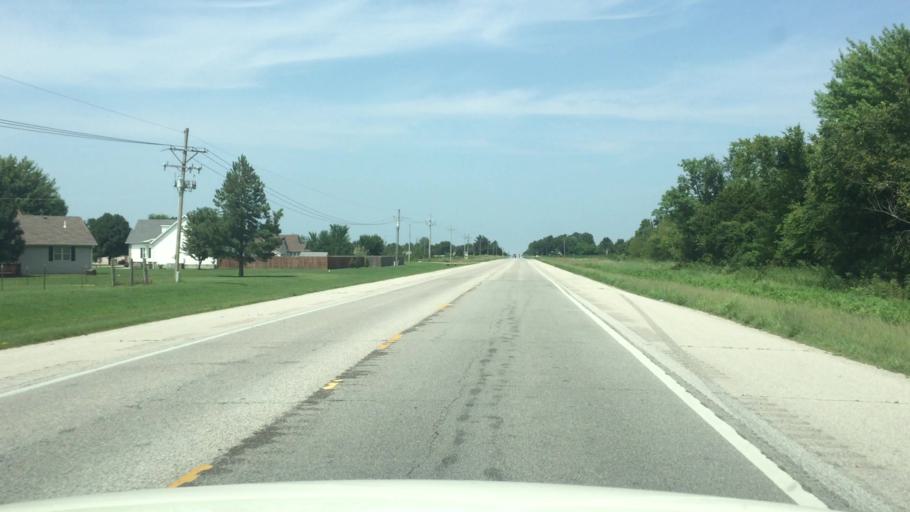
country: US
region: Kansas
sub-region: Cherokee County
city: Galena
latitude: 37.0939
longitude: -94.7044
